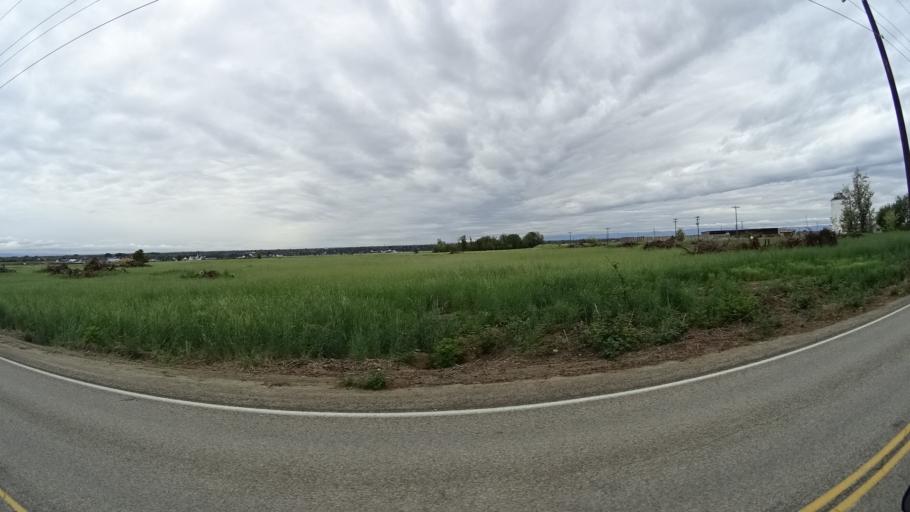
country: US
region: Idaho
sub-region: Ada County
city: Star
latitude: 43.7210
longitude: -116.4323
